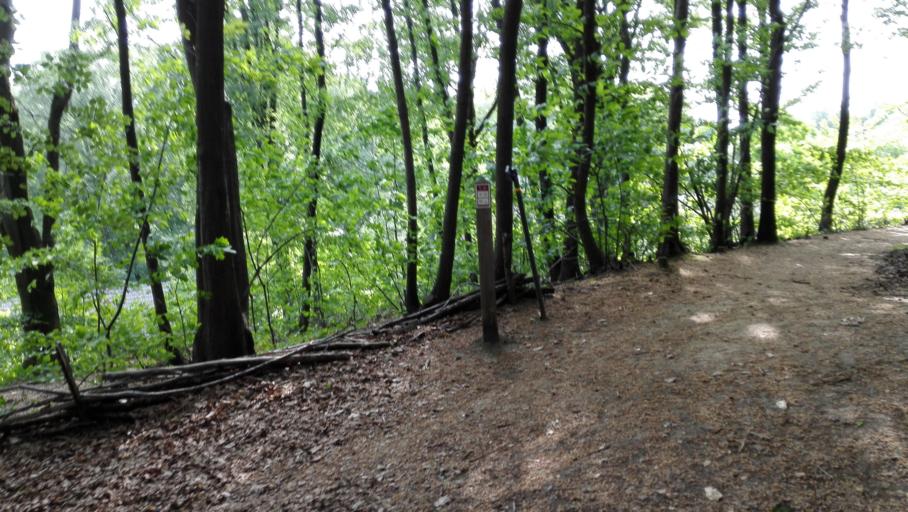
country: BE
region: Flanders
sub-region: Provincie Vlaams-Brabant
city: Holsbeek
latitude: 50.9077
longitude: 4.7688
